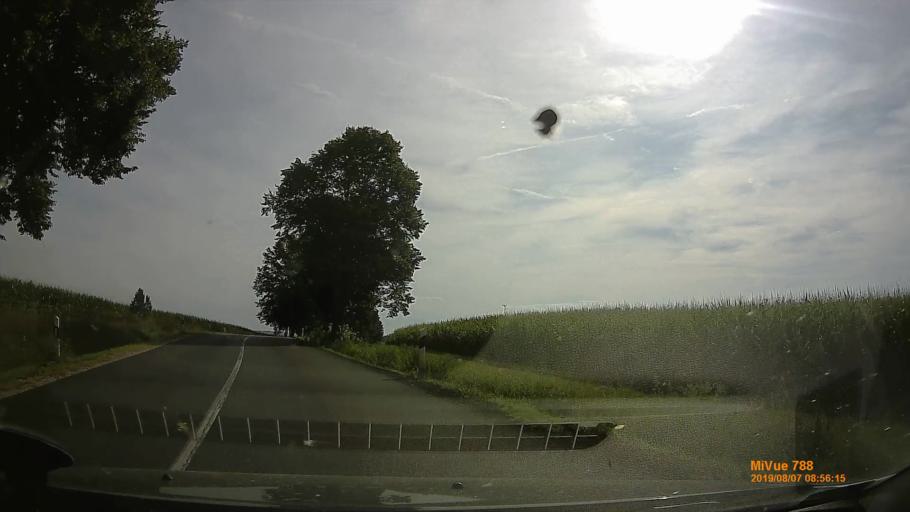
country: HU
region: Zala
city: Zalaegerszeg
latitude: 46.7313
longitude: 16.8869
